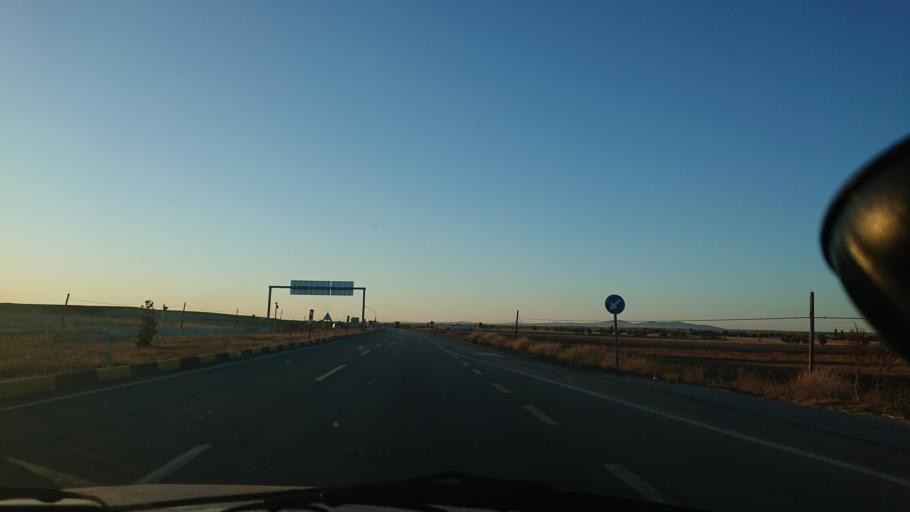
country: TR
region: Eskisehir
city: Mahmudiye
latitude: 39.5193
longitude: 30.9615
